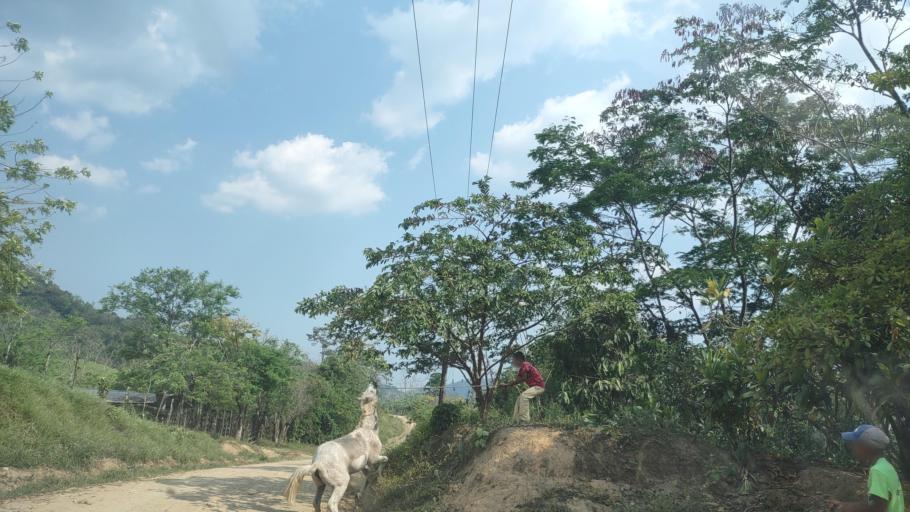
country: MX
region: Chiapas
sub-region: Tecpatan
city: Raudales Malpaso
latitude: 17.3333
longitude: -93.7510
